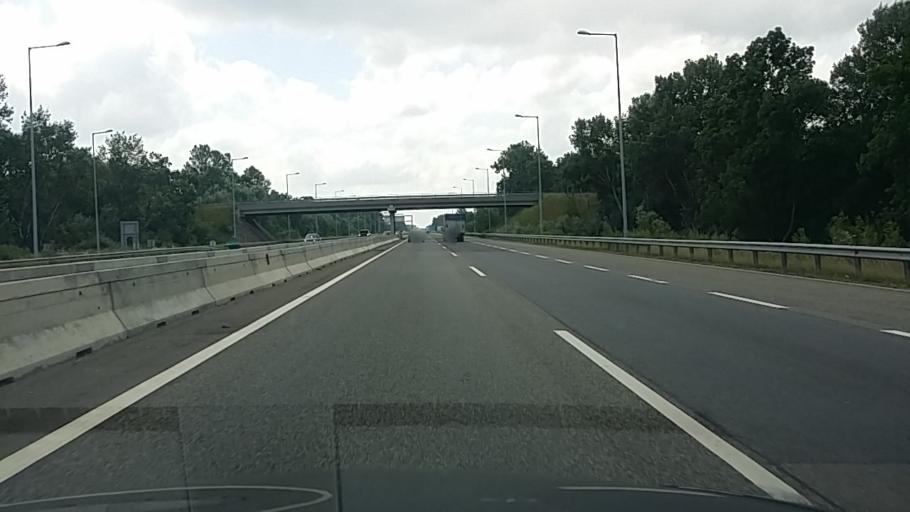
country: HU
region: Budapest
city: Budapest XVIII. keruelet
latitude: 47.3948
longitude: 19.1685
